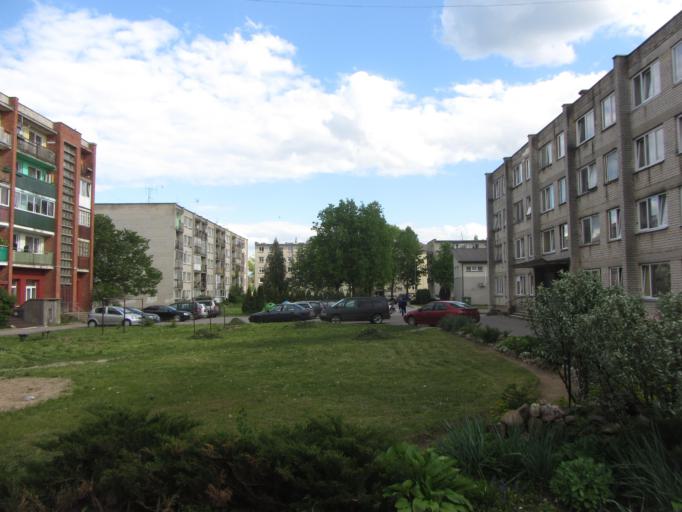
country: LT
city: Sirvintos
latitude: 55.0421
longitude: 24.9558
